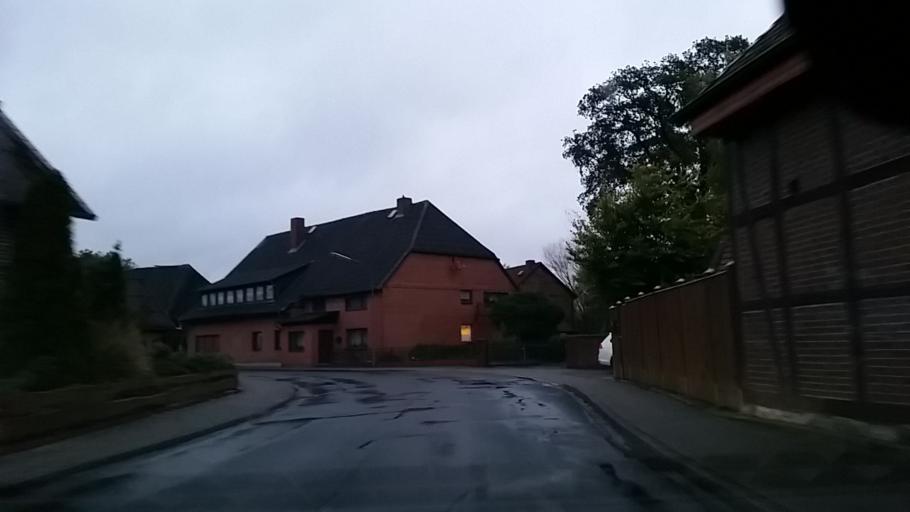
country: DE
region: Lower Saxony
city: Weyhausen
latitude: 52.4601
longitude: 10.7118
